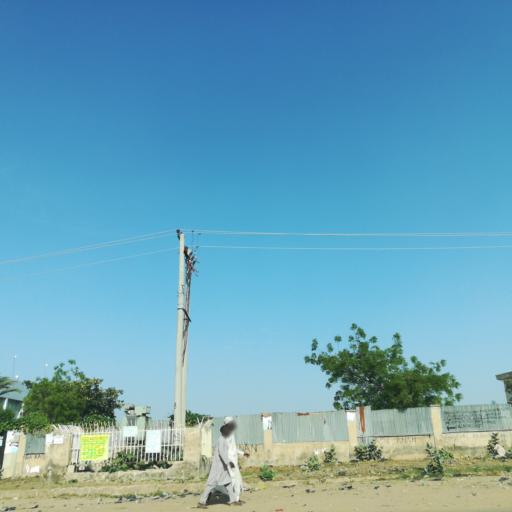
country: NG
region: Kano
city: Kano
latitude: 12.0235
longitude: 8.5021
